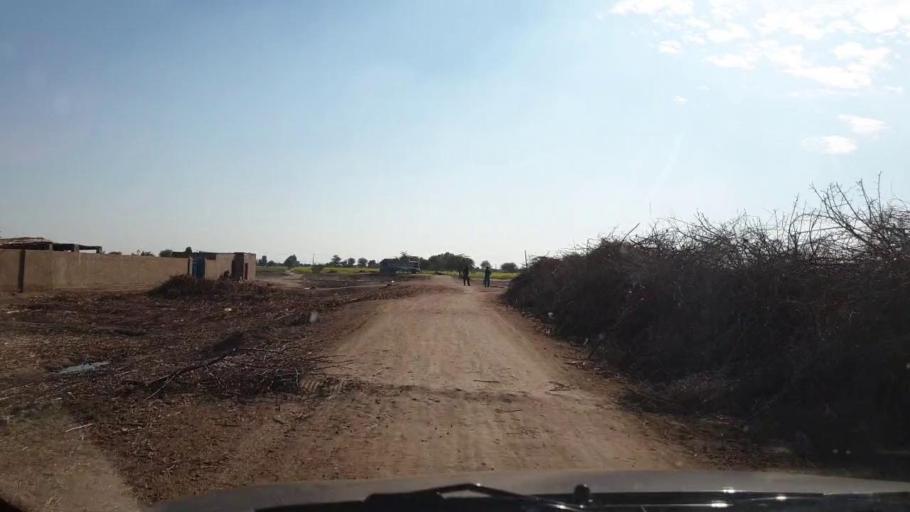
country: PK
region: Sindh
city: Sinjhoro
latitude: 26.0097
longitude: 68.8295
